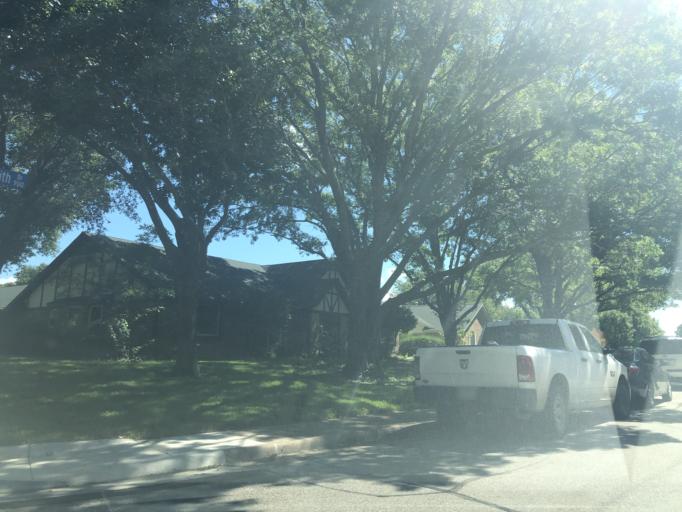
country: US
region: Texas
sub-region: Dallas County
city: Duncanville
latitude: 32.6387
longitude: -96.9300
